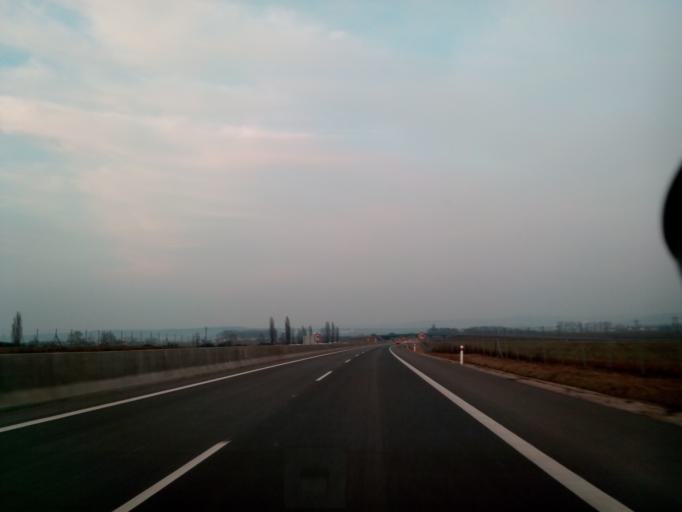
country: SK
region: Kosicky
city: Kosice
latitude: 48.6391
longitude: 21.2618
